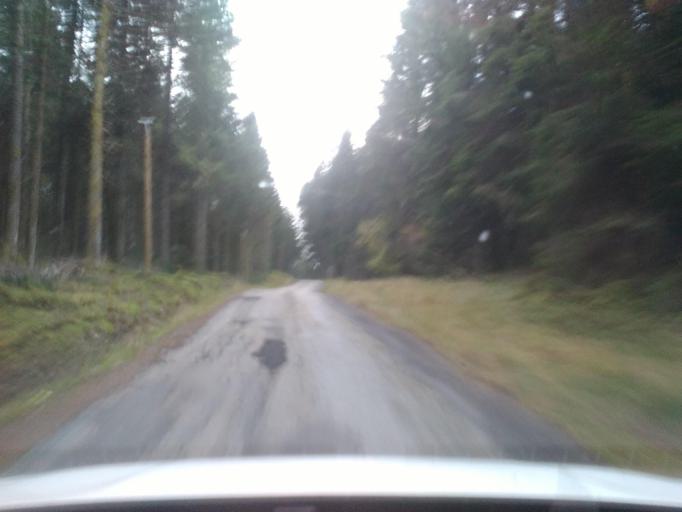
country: FR
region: Lorraine
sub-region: Departement des Vosges
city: Gerardmer
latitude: 48.0869
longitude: 6.8534
